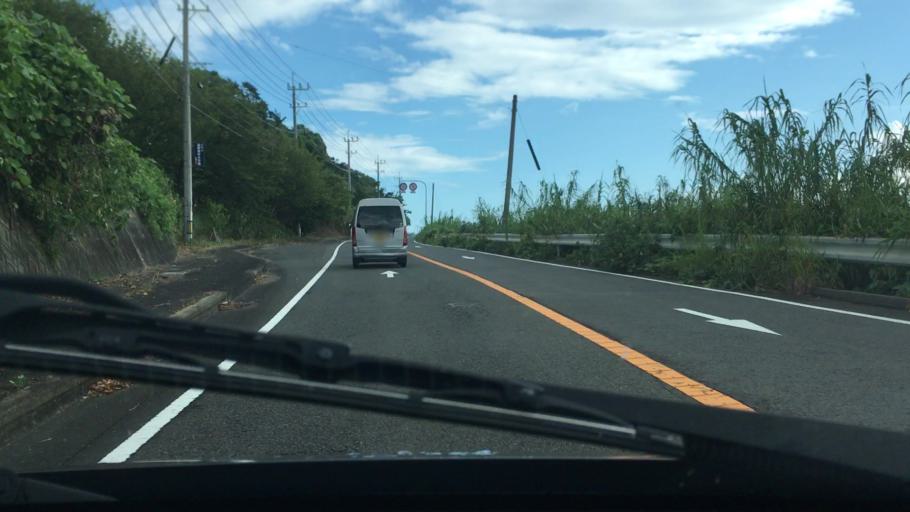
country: JP
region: Nagasaki
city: Togitsu
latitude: 32.8731
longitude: 129.6784
